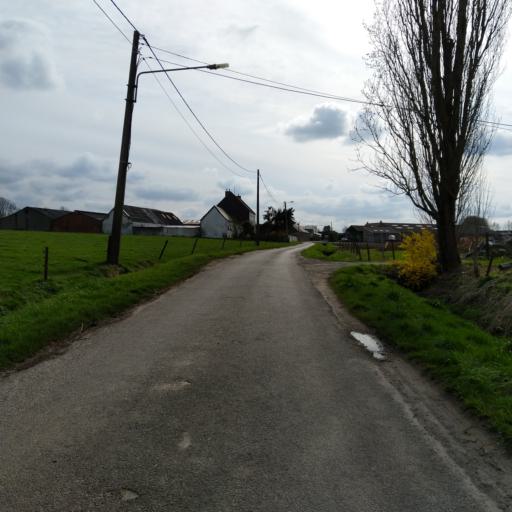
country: BE
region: Wallonia
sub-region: Province du Hainaut
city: Soignies
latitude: 50.5435
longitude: 4.0640
